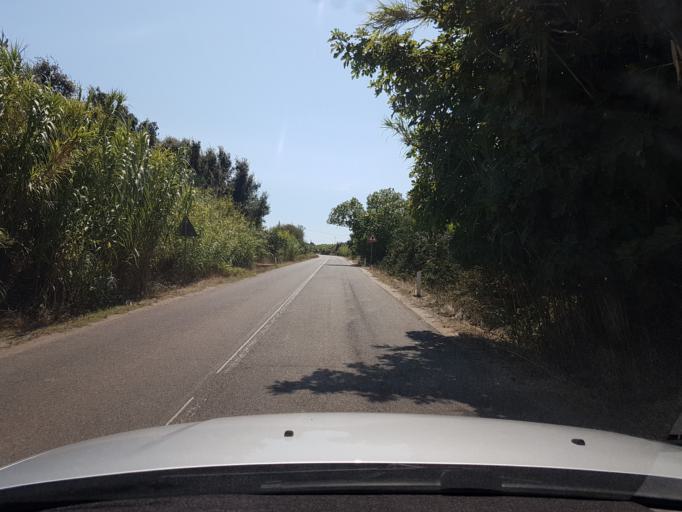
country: IT
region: Sardinia
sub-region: Provincia di Oristano
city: Solanas
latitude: 39.9453
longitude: 8.5508
